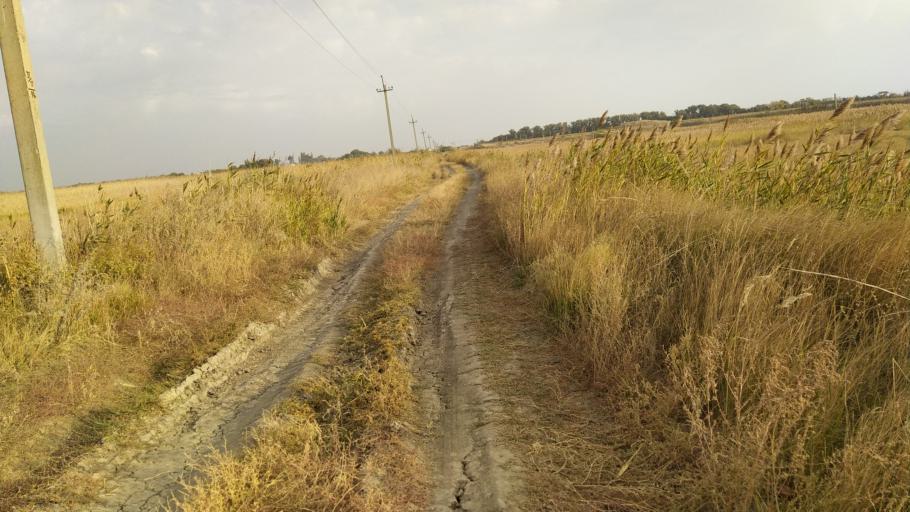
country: RU
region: Rostov
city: Kuleshovka
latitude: 47.1139
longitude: 39.6058
